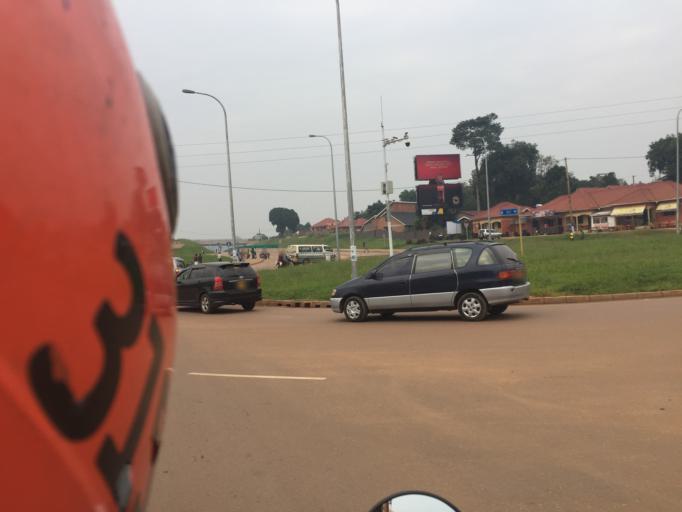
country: UG
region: Central Region
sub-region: Kampala District
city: Kampala
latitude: 0.2392
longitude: 32.6210
